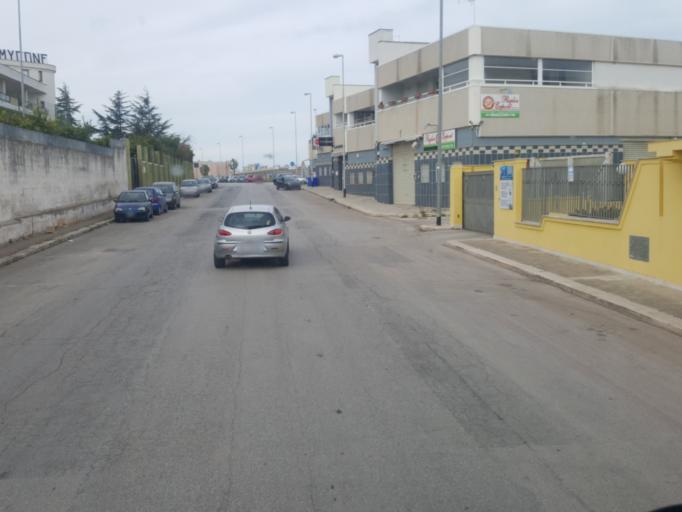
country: IT
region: Apulia
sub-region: Provincia di Barletta - Andria - Trani
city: Bisceglie
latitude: 41.2270
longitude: 16.5043
